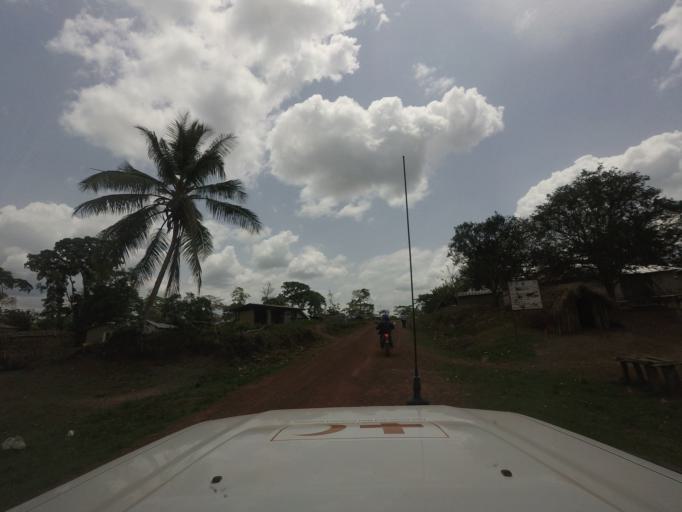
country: LR
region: Bong
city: Gbarnga
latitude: 7.1593
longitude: -9.2130
